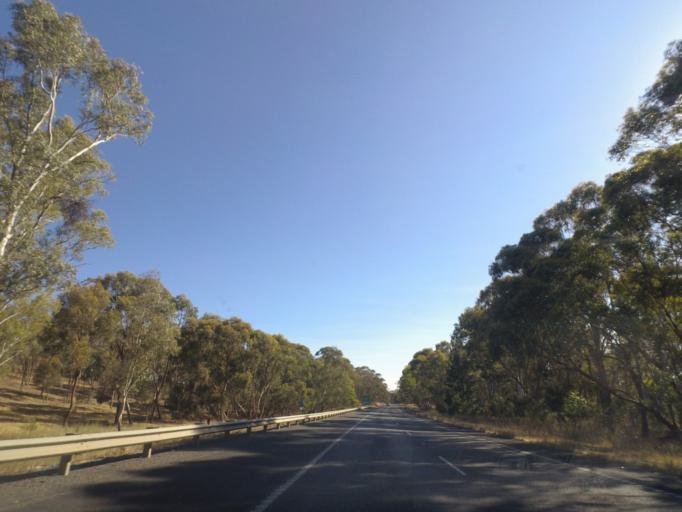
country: AU
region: Victoria
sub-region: Murrindindi
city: Kinglake West
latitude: -37.1728
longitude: 145.0749
